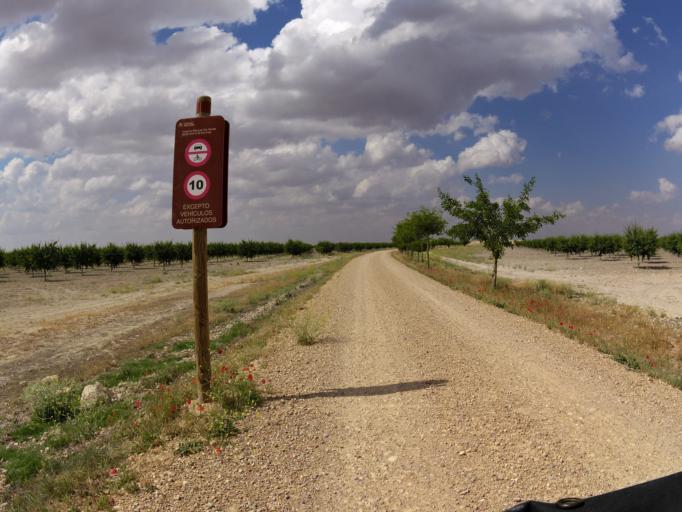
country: ES
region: Castille-La Mancha
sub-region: Provincia de Albacete
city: Albacete
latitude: 38.9534
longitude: -1.9791
